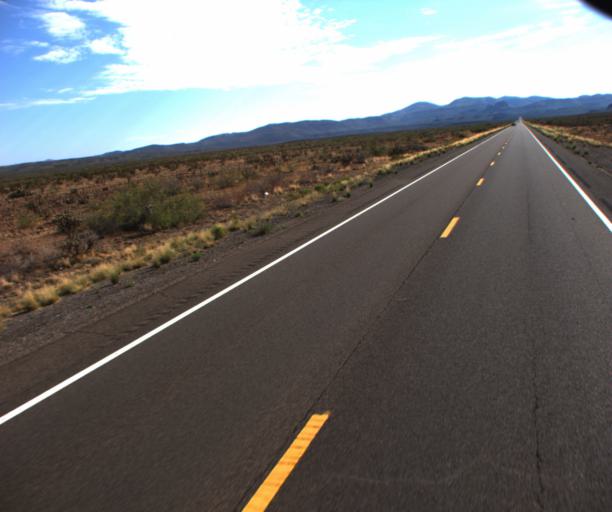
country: US
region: Arizona
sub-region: Graham County
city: Safford
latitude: 32.8194
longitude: -109.4795
